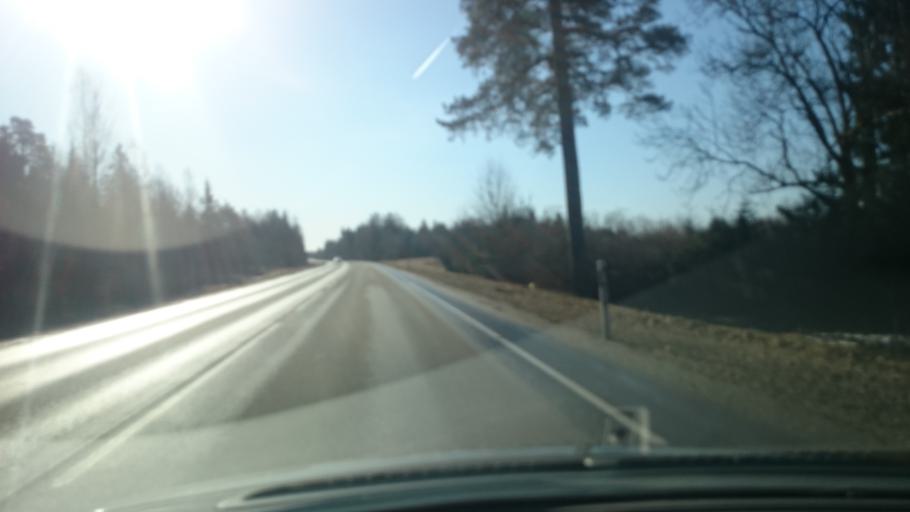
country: EE
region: Raplamaa
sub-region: Kohila vald
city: Kohila
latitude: 59.2431
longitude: 24.7527
